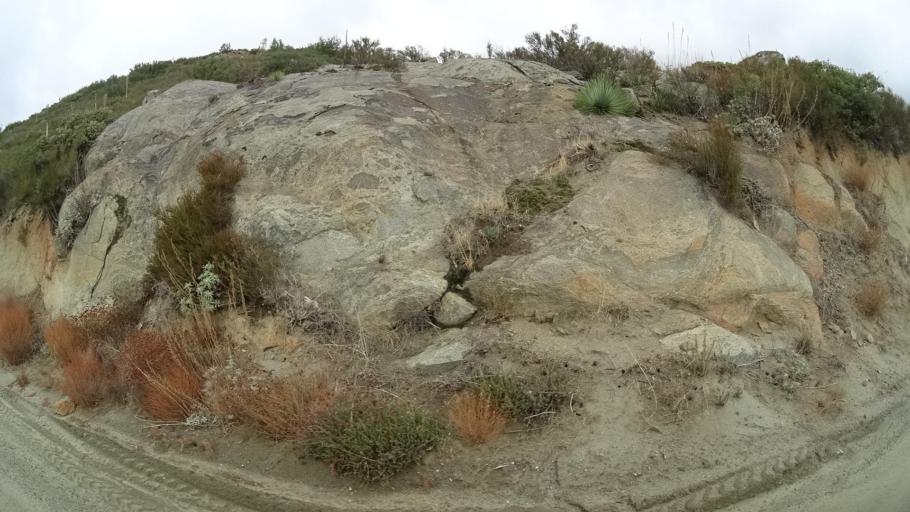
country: US
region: California
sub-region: San Diego County
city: Descanso
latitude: 32.9505
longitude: -116.6388
